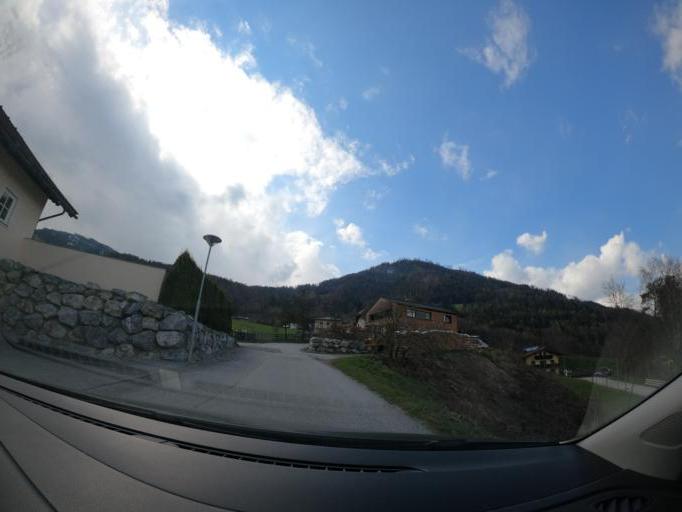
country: AT
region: Salzburg
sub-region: Politischer Bezirk Sankt Johann im Pongau
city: Bischofshofen
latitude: 47.4171
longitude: 13.2135
